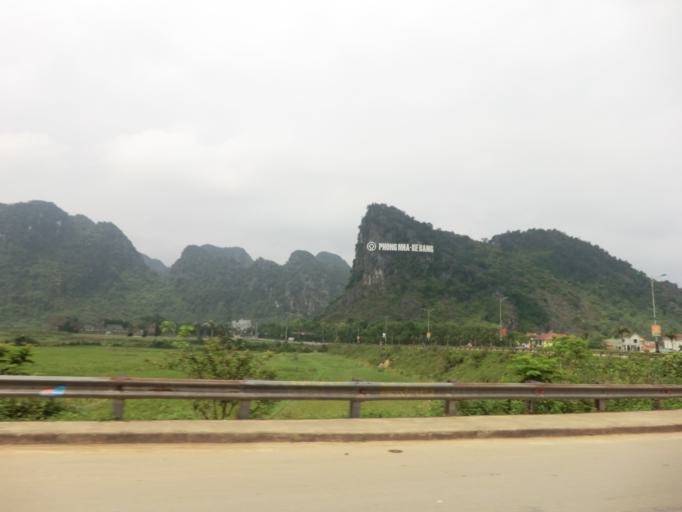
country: VN
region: Quang Binh
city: Ba Don
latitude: 17.6108
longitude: 106.3196
